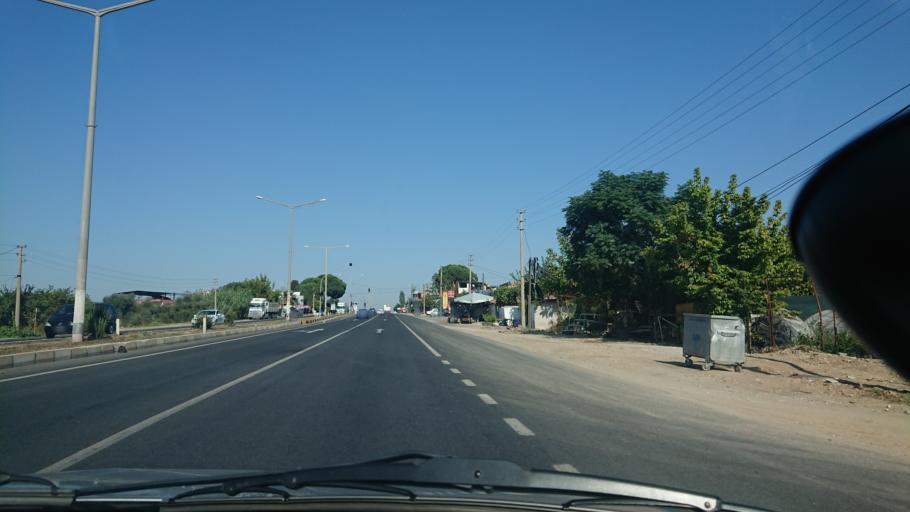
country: TR
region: Manisa
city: Ahmetli
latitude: 38.5000
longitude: 27.8689
